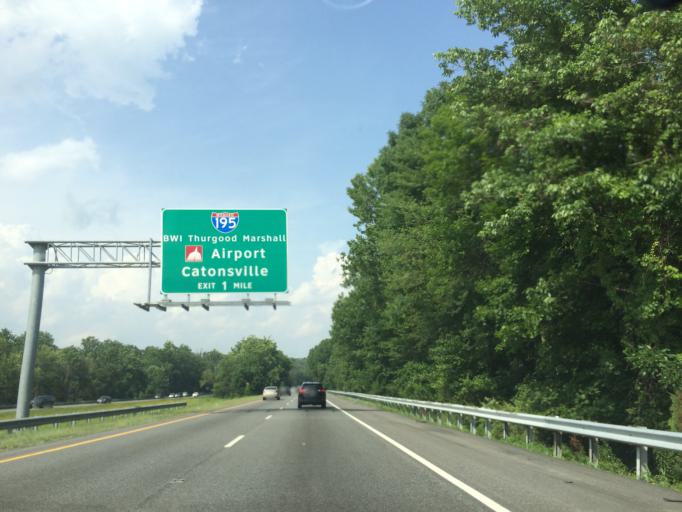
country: US
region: Maryland
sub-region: Howard County
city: Hanover
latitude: 39.1887
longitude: -76.7141
